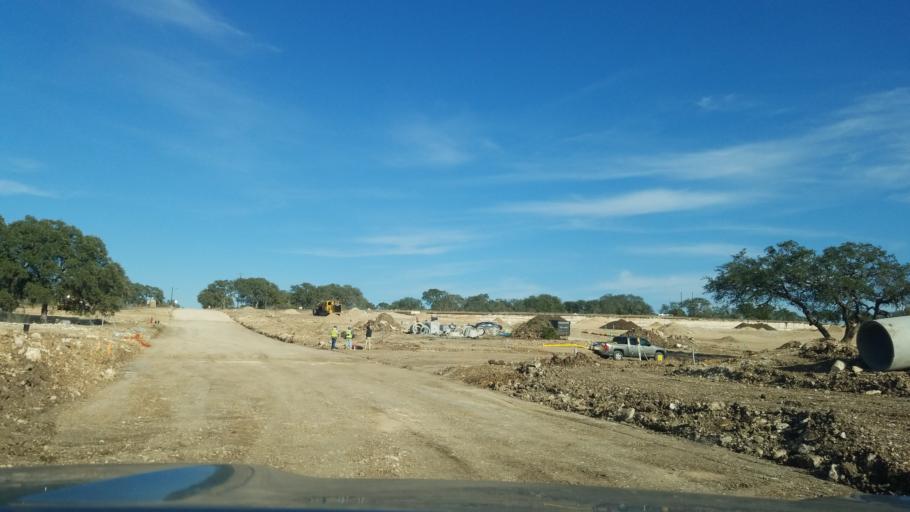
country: US
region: Texas
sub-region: Comal County
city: Canyon Lake
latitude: 29.7859
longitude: -98.2882
